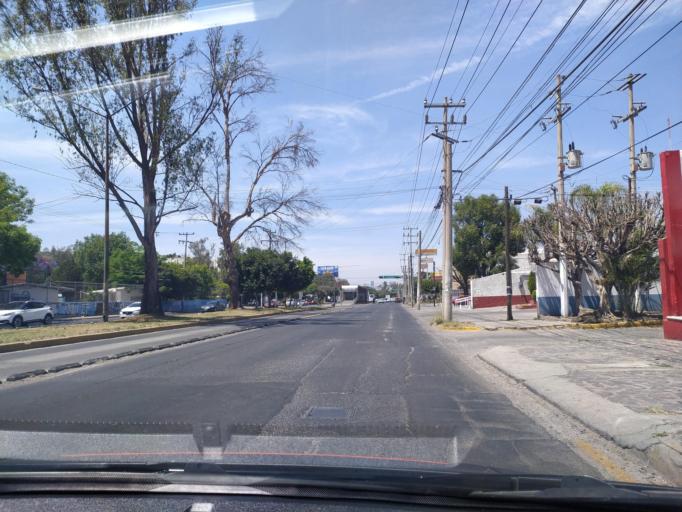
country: MX
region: Jalisco
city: Las Pintas de Arriba
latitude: 20.6202
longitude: -103.3455
